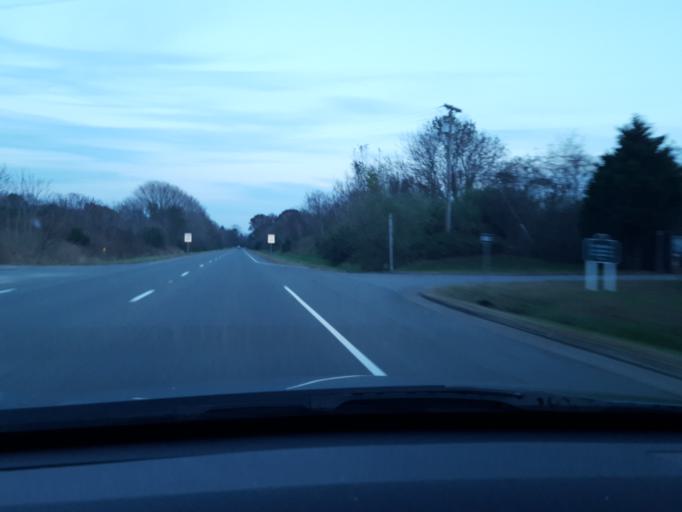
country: US
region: Virginia
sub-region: King George County
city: King George
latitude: 38.1605
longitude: -77.1938
